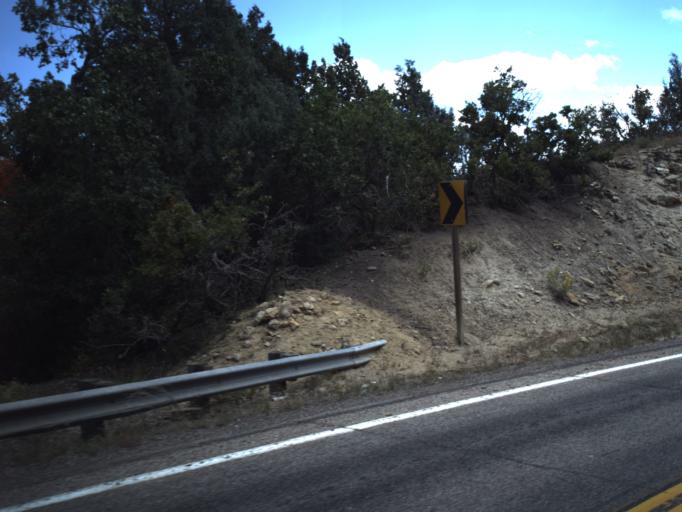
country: US
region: Utah
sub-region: Garfield County
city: Panguitch
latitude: 37.4905
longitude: -112.5280
